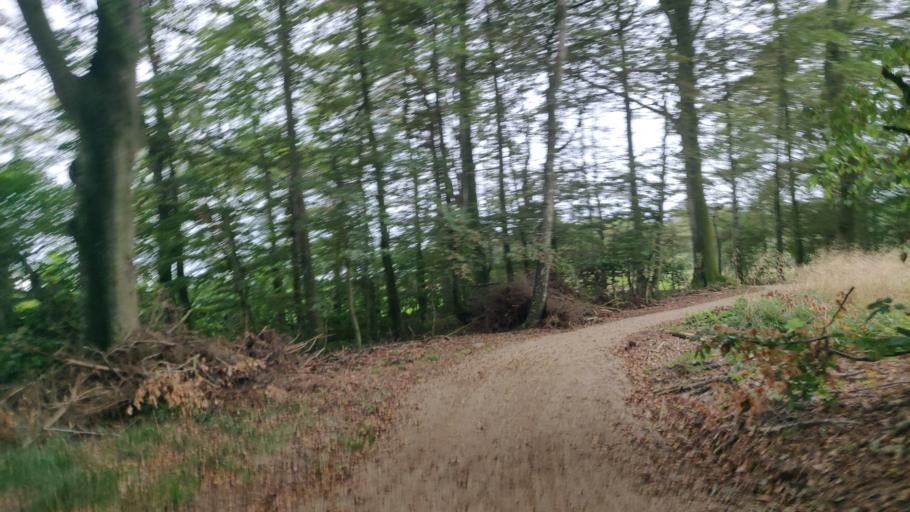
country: DK
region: South Denmark
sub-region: Kolding Kommune
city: Lunderskov
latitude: 55.5390
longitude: 9.3487
